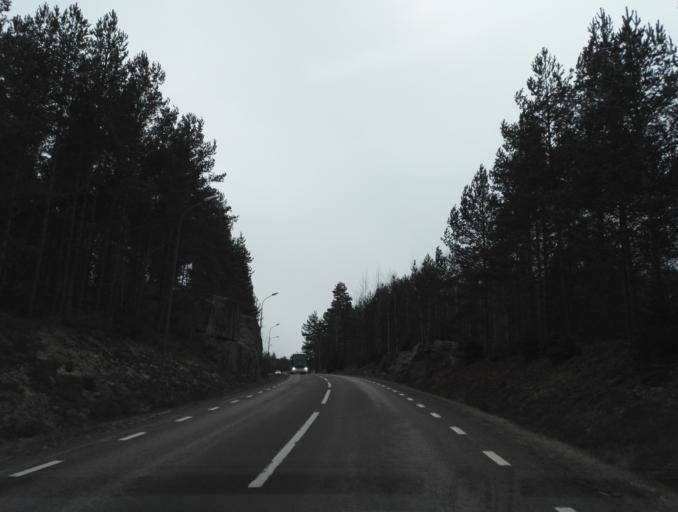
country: SE
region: Kalmar
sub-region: Hultsfreds Kommun
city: Virserum
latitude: 57.3293
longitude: 15.5855
